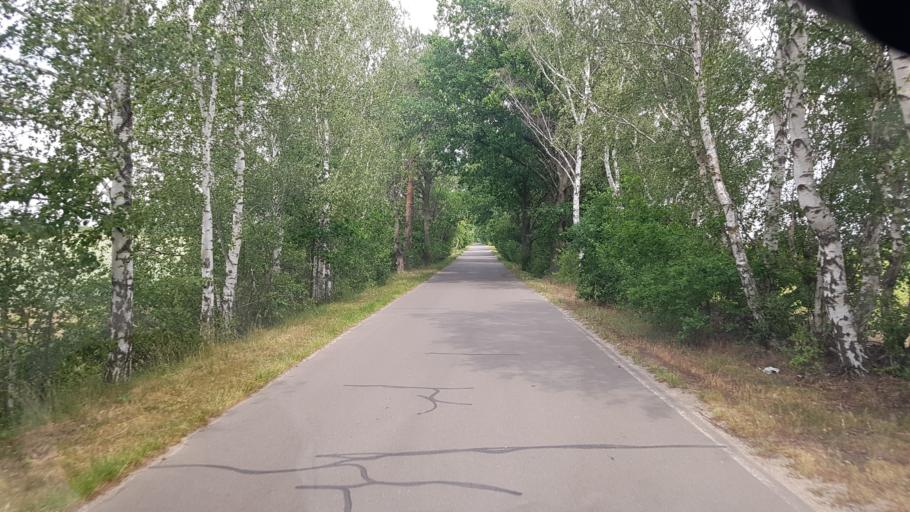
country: DE
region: Brandenburg
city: Dahme
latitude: 51.8457
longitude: 13.4433
